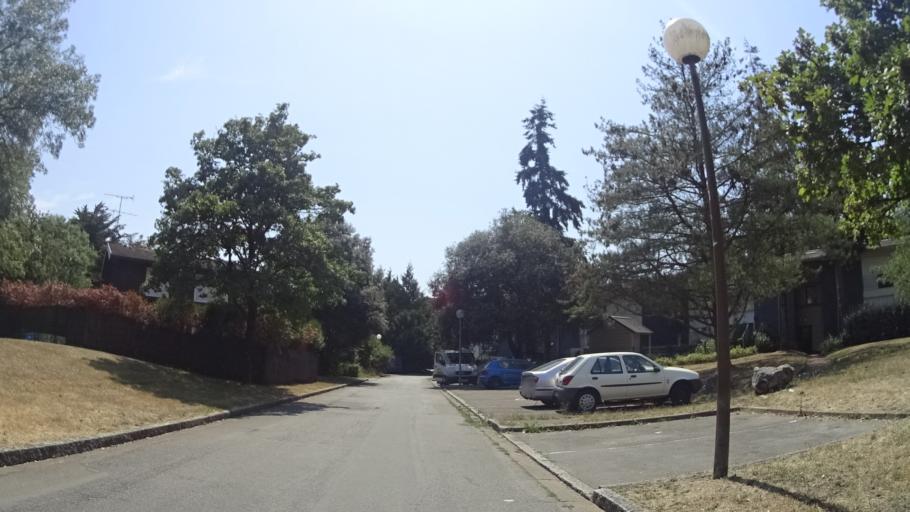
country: FR
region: Pays de la Loire
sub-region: Departement de la Loire-Atlantique
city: Savenay
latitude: 47.3626
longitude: -1.9350
